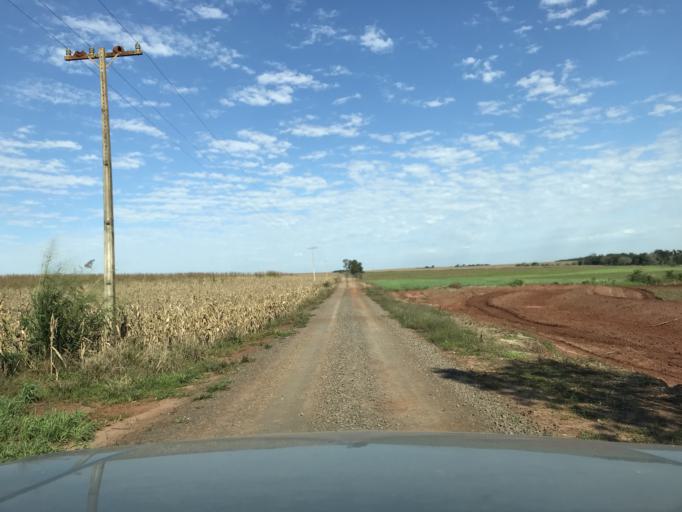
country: BR
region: Parana
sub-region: Palotina
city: Palotina
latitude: -24.1639
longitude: -53.7498
